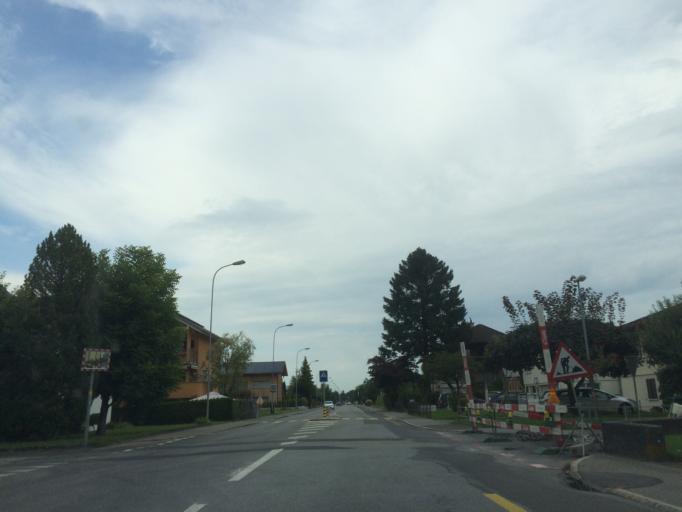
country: LI
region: Ruggell
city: Ruggell
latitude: 47.2361
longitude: 9.5201
